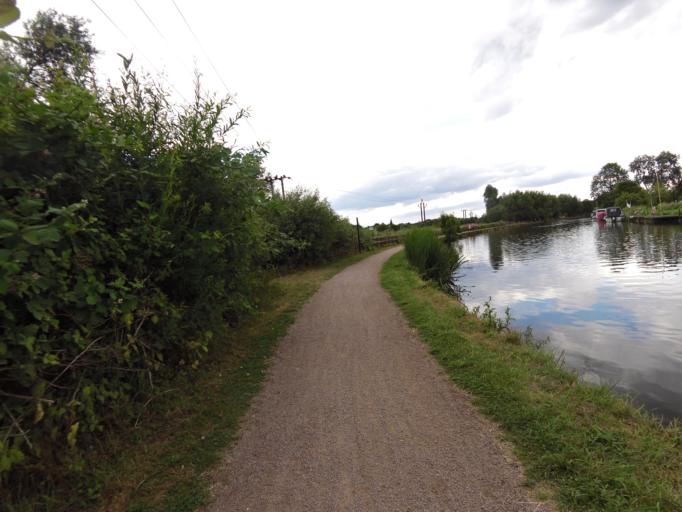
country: GB
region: England
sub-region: Hertfordshire
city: Broxbourne
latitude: 51.7351
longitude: -0.0138
